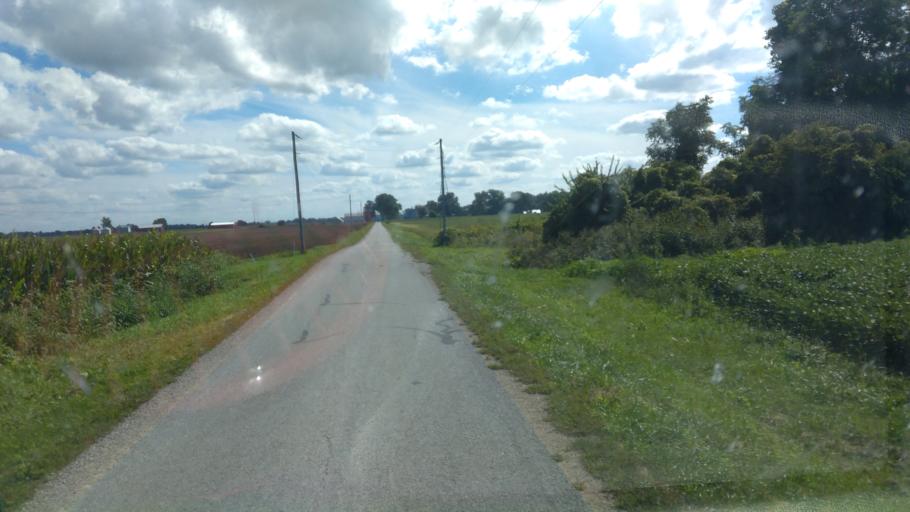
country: US
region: Ohio
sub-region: Huron County
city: Bellevue
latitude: 41.3932
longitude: -82.8823
